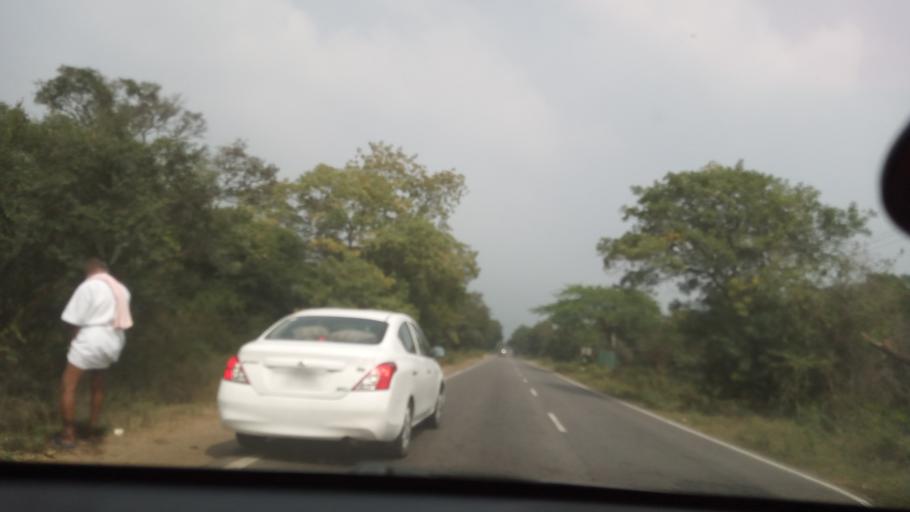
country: IN
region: Tamil Nadu
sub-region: Erode
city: Sathyamangalam
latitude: 11.5582
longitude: 77.1369
